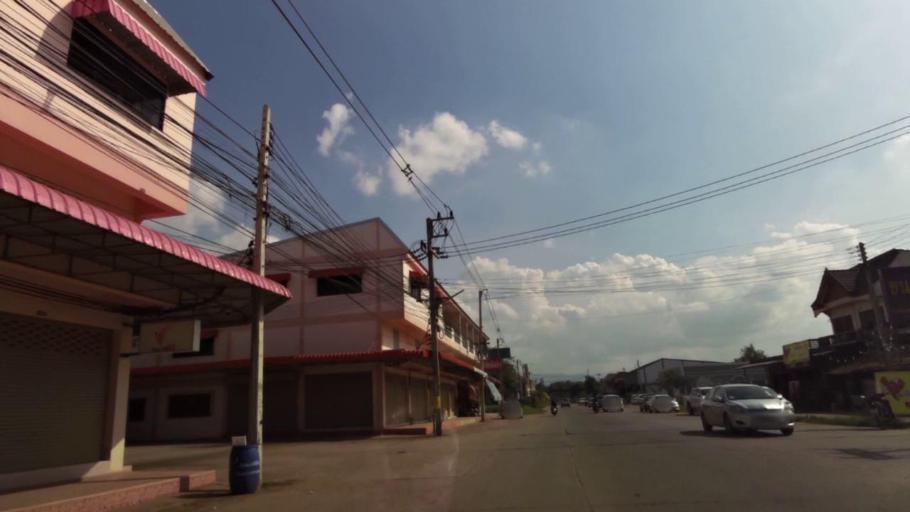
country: TH
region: Phrae
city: Phrae
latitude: 18.1207
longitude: 100.1544
